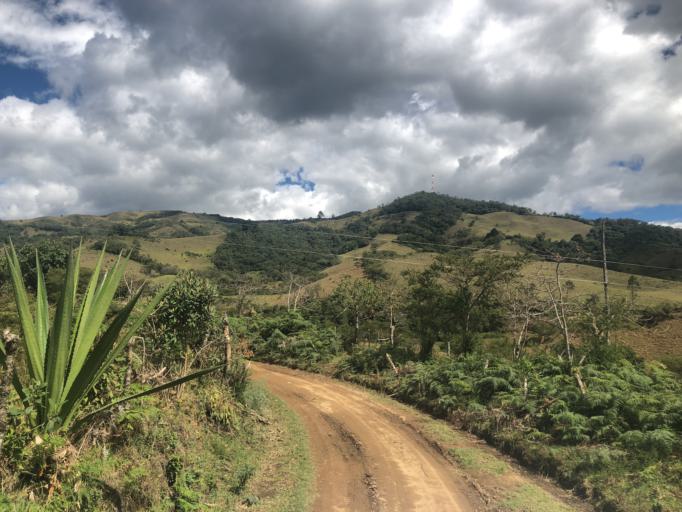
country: CO
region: Cauca
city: Silvia
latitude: 2.6831
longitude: -76.4388
